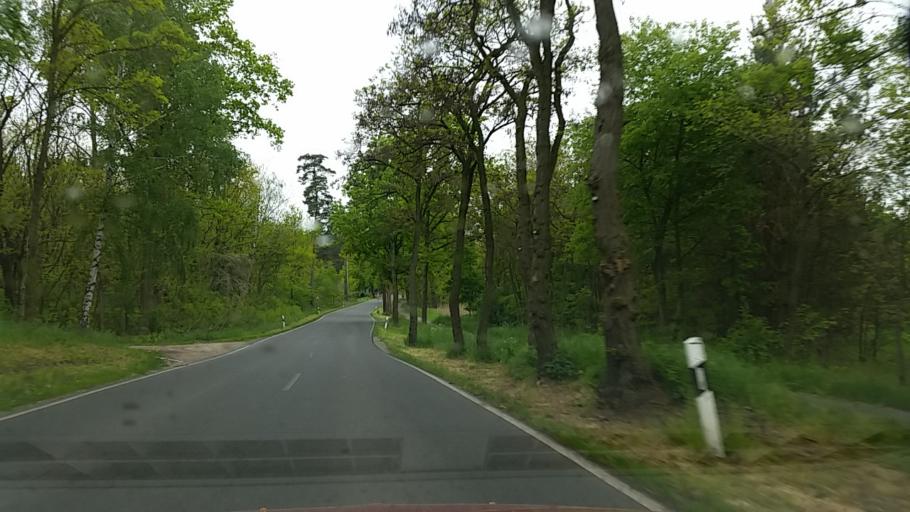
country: DE
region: Brandenburg
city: Reichenwalde
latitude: 52.2692
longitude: 14.0152
